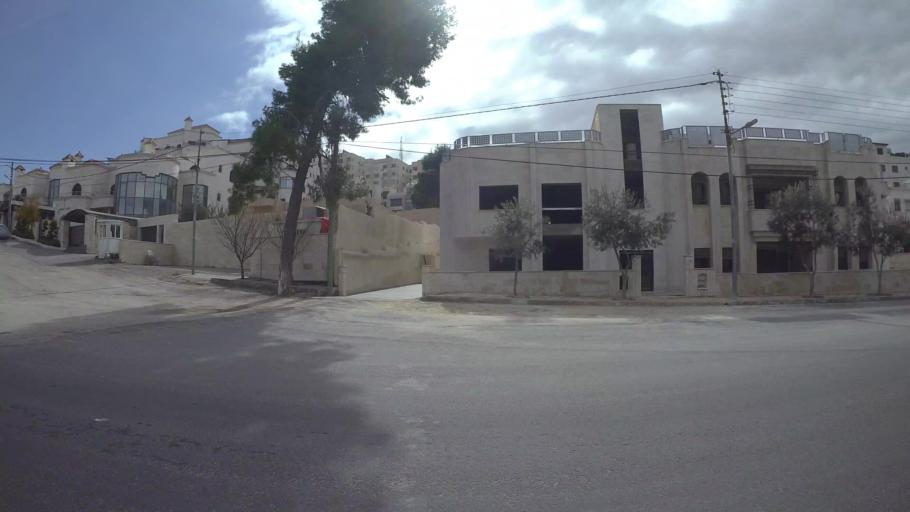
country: JO
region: Amman
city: Al Jubayhah
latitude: 32.0077
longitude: 35.8382
